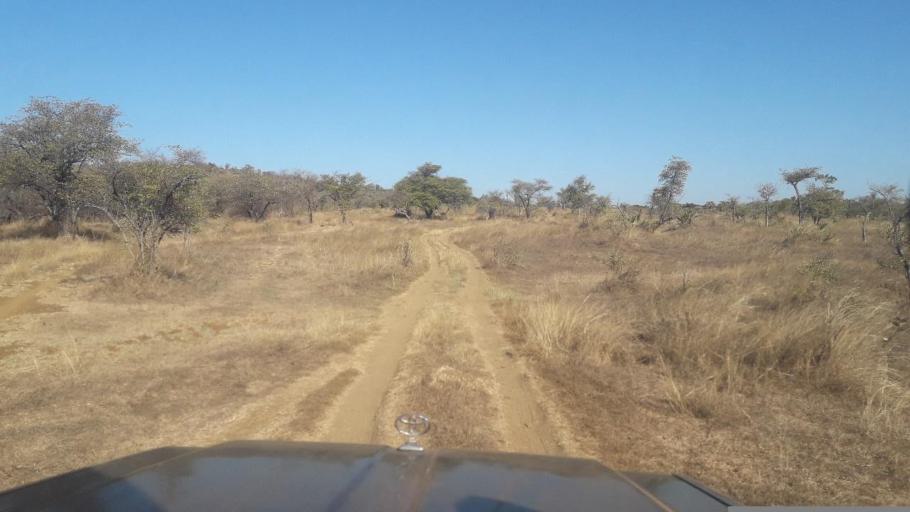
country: MG
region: Boeny
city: Sitampiky
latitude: -16.3887
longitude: 45.5913
